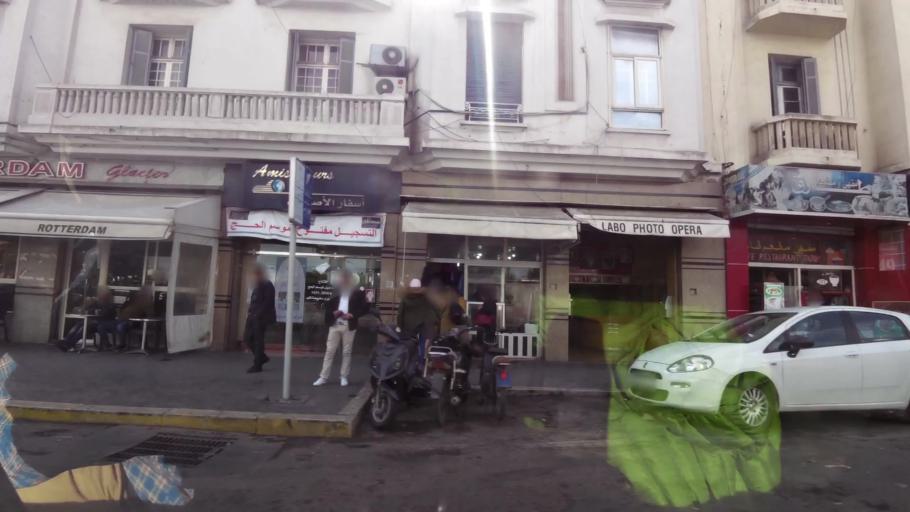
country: MA
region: Grand Casablanca
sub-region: Casablanca
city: Casablanca
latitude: 33.5949
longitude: -7.6201
